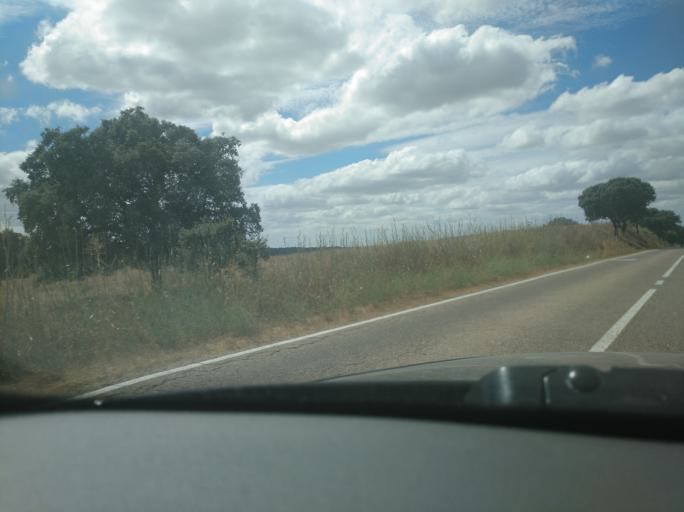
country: PT
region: Portalegre
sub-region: Arronches
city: Arronches
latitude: 39.0371
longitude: -7.4160
